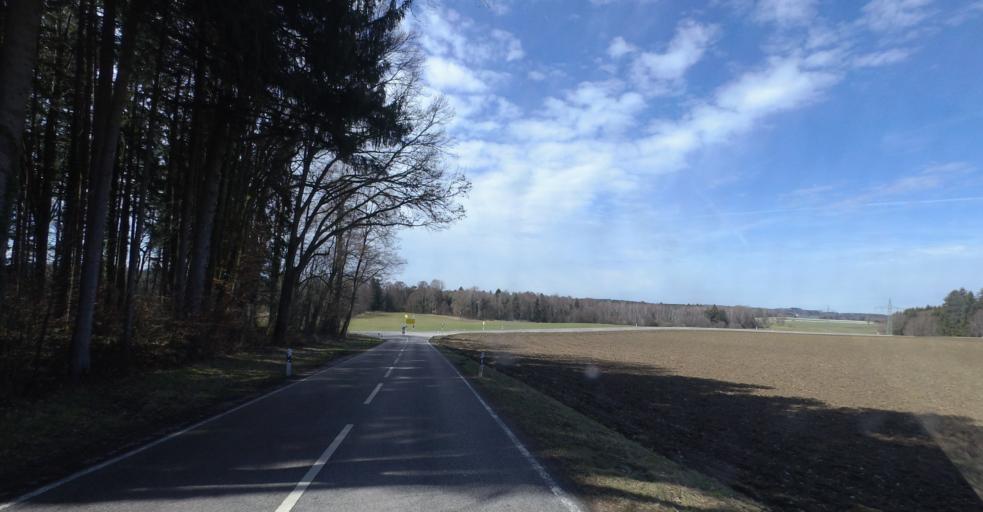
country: DE
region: Bavaria
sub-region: Upper Bavaria
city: Seeon-Seebruck
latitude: 47.9338
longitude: 12.4986
